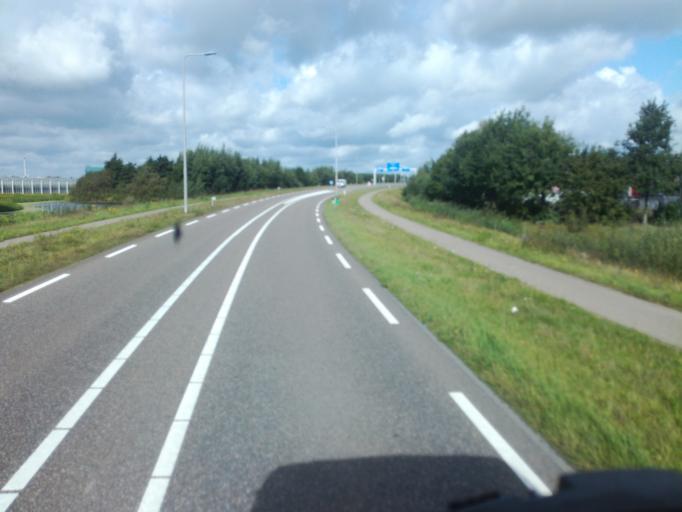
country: NL
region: Limburg
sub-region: Gemeente Peel en Maas
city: Maasbree
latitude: 51.3907
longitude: 6.0856
